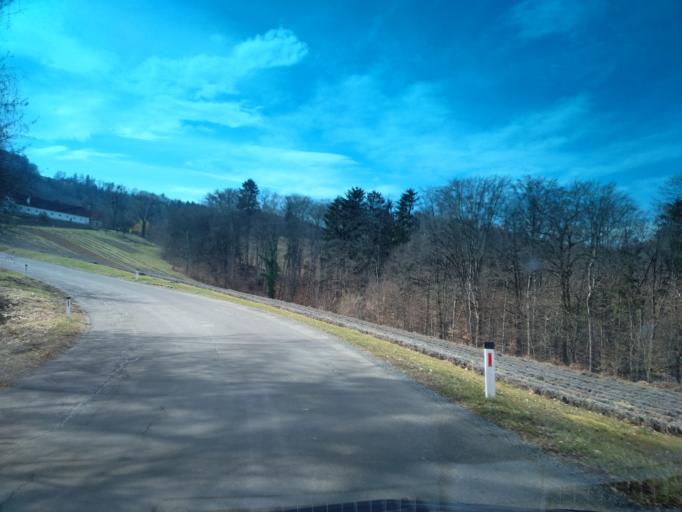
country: AT
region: Styria
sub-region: Politischer Bezirk Leibnitz
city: Kitzeck im Sausal
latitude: 46.7932
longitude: 15.4379
